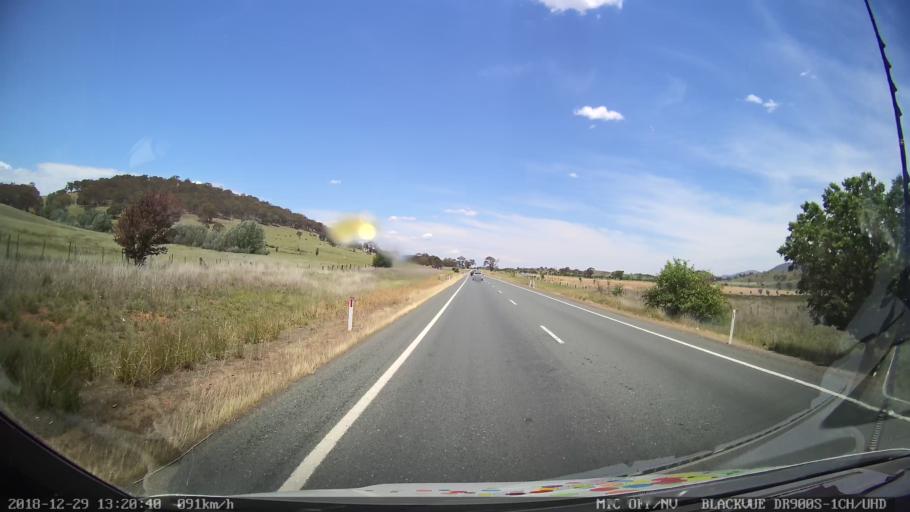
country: AU
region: Australian Capital Territory
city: Macarthur
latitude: -35.7819
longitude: 149.1619
